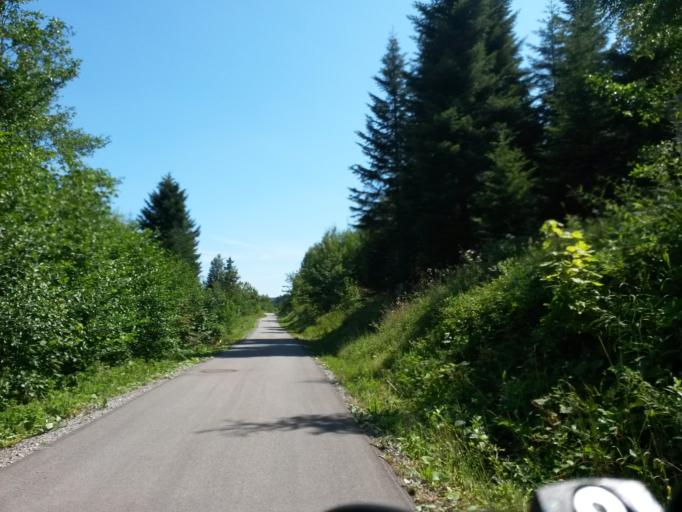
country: DE
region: Baden-Wuerttemberg
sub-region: Karlsruhe Region
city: Enzklosterle
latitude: 48.6904
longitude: 8.5021
